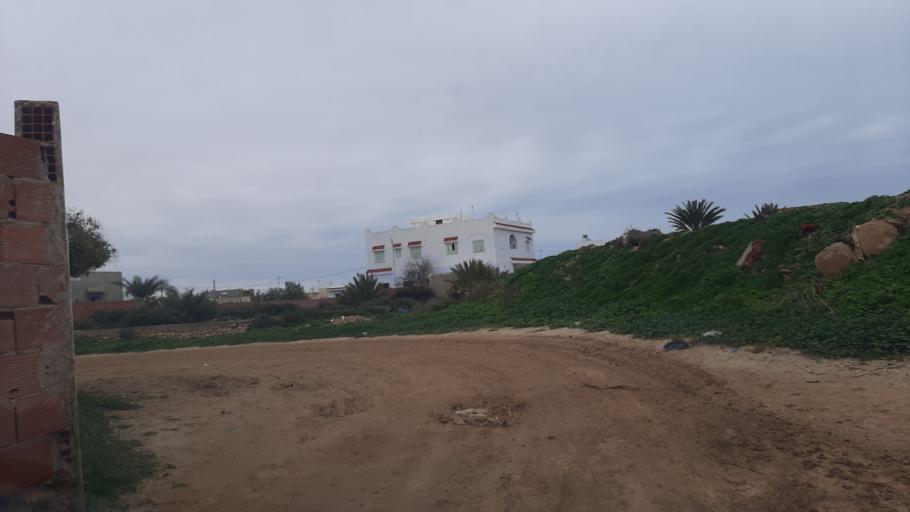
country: TN
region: Safaqis
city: Al Qarmadah
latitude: 34.7984
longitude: 10.8565
